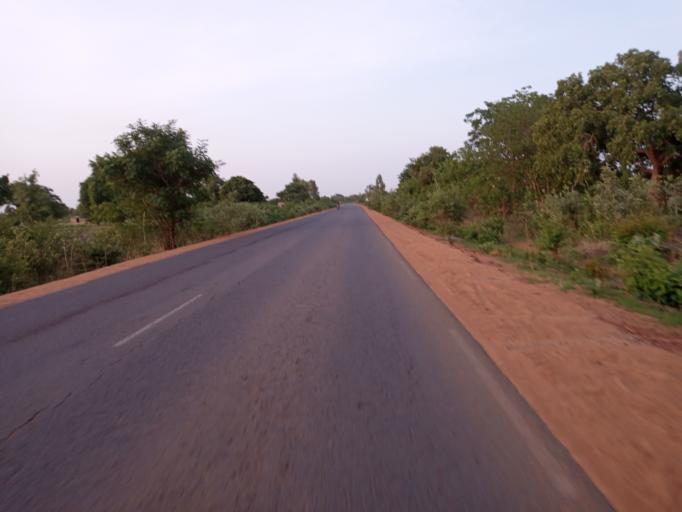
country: ML
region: Bamako
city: Bamako
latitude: 12.2926
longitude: -8.1672
